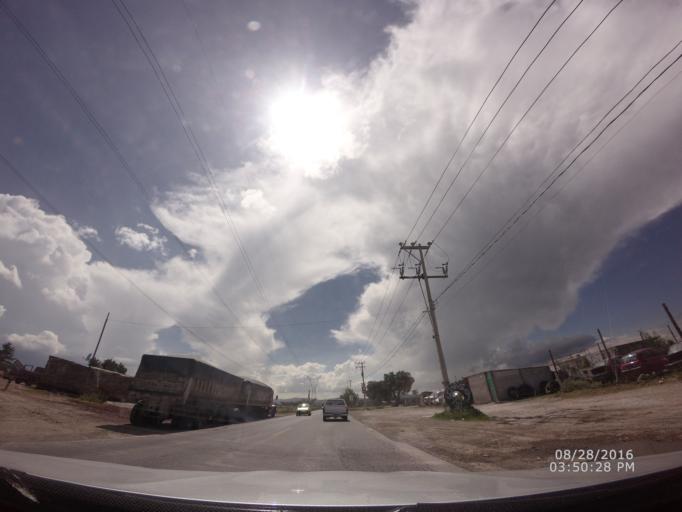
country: MX
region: Hidalgo
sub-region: Mineral de la Reforma
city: Rinconada de los Angeles
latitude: 20.0372
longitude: -98.7338
